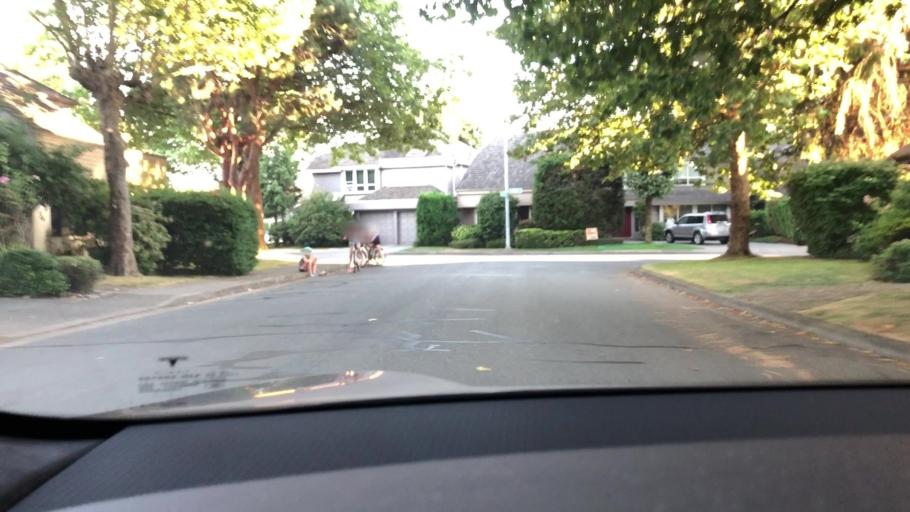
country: CA
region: British Columbia
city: Richmond
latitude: 49.1463
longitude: -123.1667
